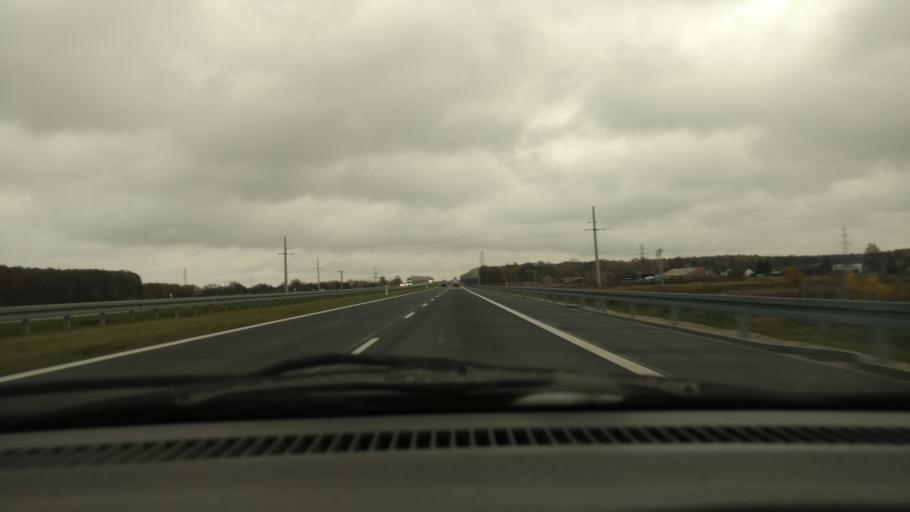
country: PL
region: Lodz Voivodeship
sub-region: Powiat pabianicki
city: Dobron
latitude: 51.6071
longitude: 19.3101
